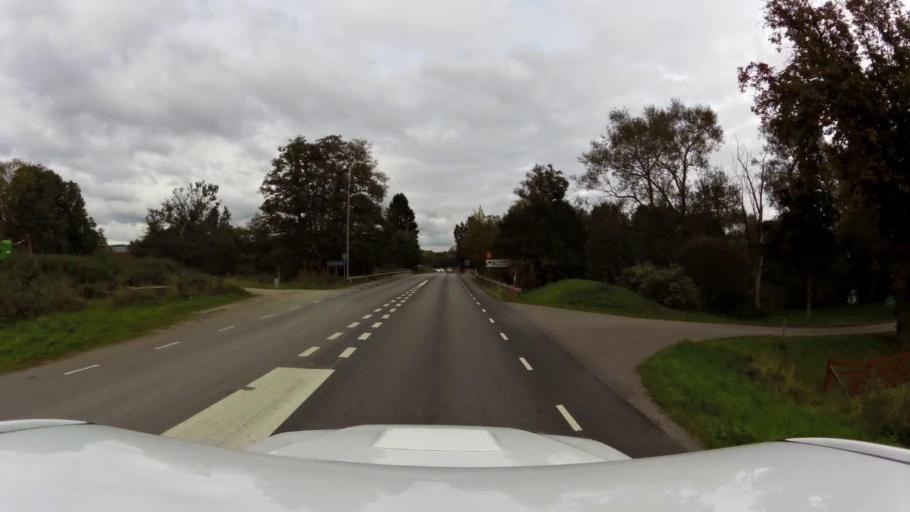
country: SE
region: OEstergoetland
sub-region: Linkopings Kommun
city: Berg
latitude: 58.5006
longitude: 15.5370
